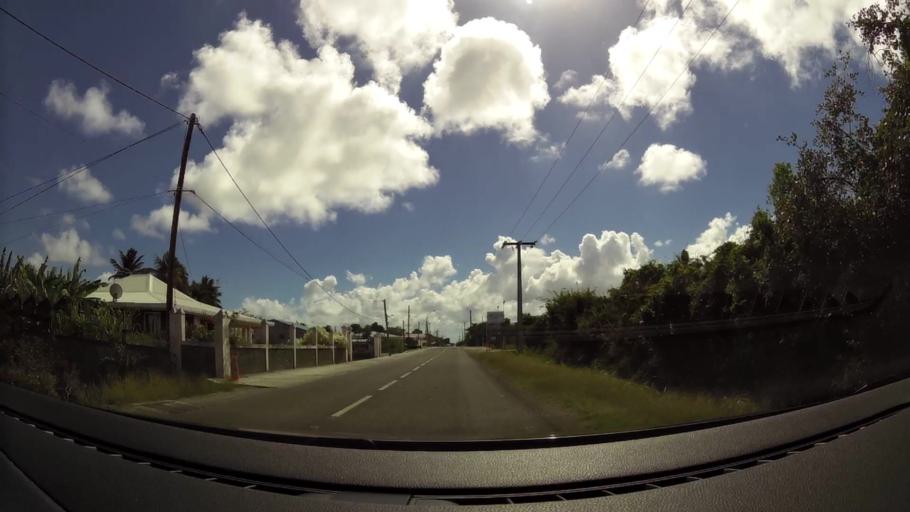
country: GP
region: Guadeloupe
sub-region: Guadeloupe
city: Petit-Canal
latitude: 16.4253
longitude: -61.4754
